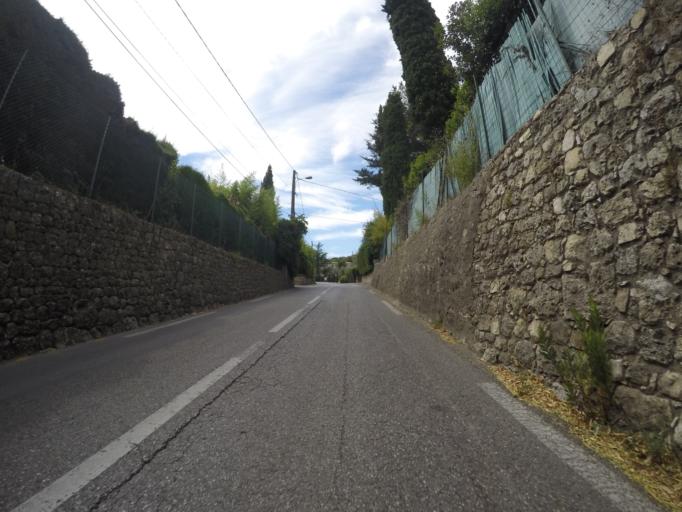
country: FR
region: Provence-Alpes-Cote d'Azur
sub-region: Departement des Alpes-Maritimes
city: Mougins
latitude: 43.6033
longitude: 6.9983
